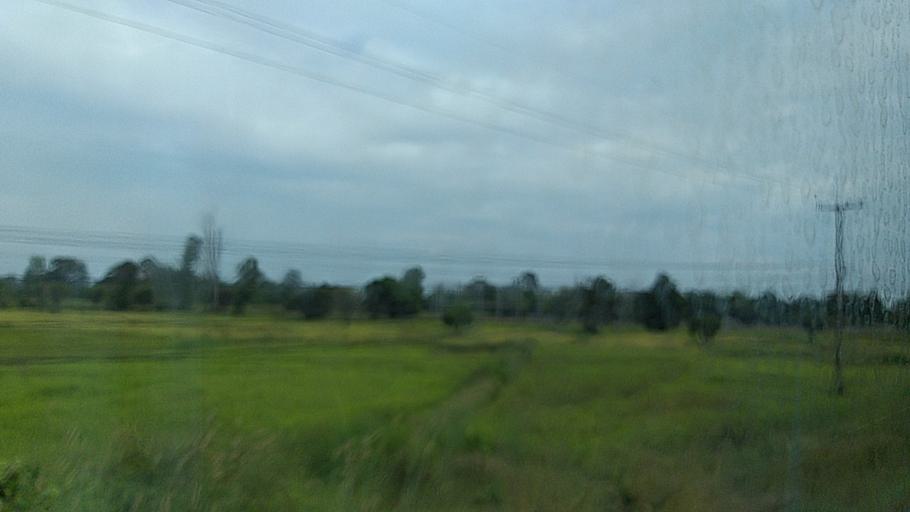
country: TH
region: Roi Et
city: Changhan
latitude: 16.1033
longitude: 103.5218
